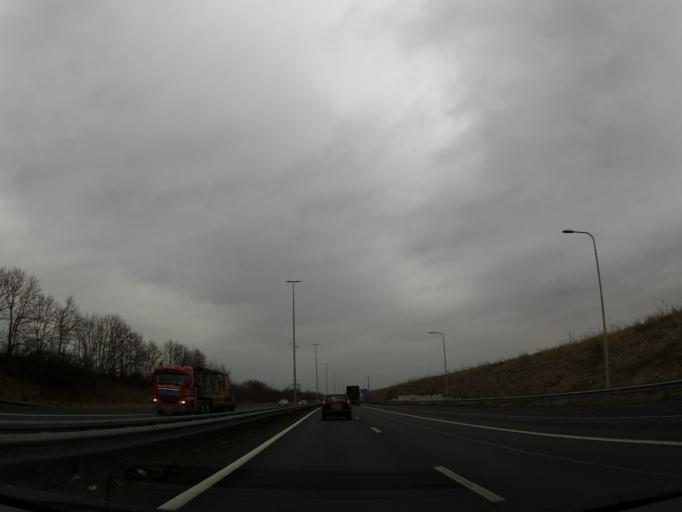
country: BE
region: Flanders
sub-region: Provincie Limburg
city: Maaseik
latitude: 51.0817
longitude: 5.8287
